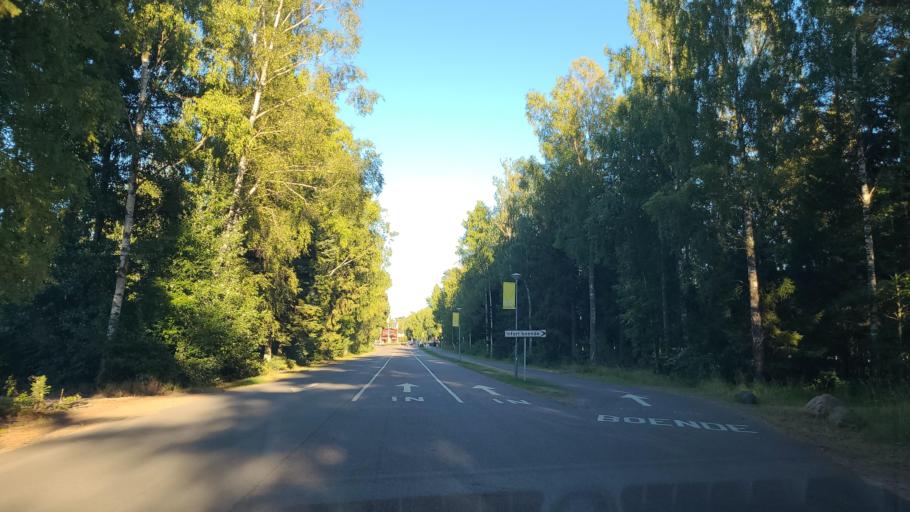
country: SE
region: Kalmar
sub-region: Borgholms Kommun
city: Borgholm
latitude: 57.2752
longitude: 17.0446
